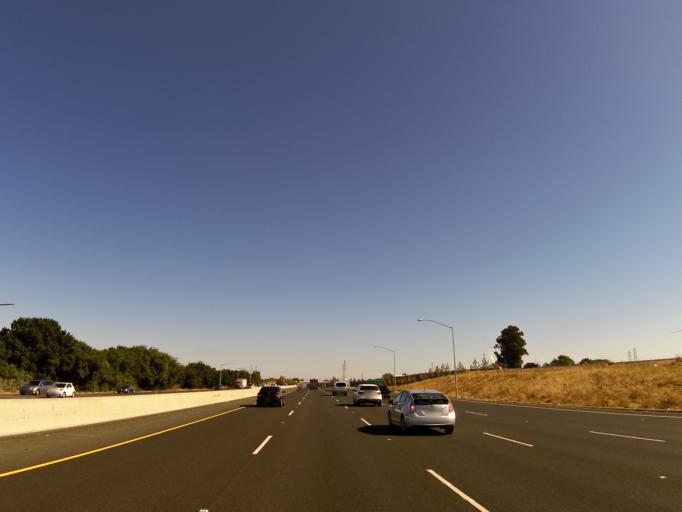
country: US
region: California
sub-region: Solano County
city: Green Valley
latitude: 38.2352
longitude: -122.1030
